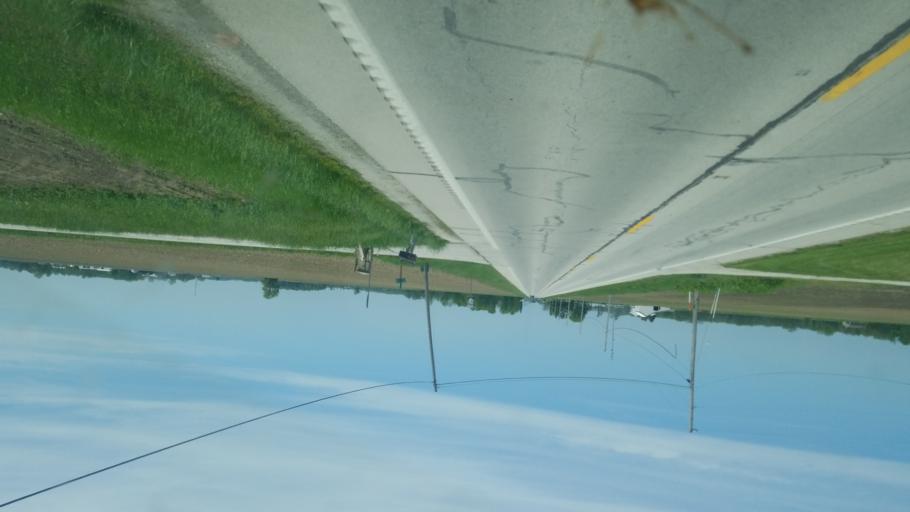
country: US
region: Ohio
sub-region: Seneca County
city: Tiffin
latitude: 41.2181
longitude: -83.1675
